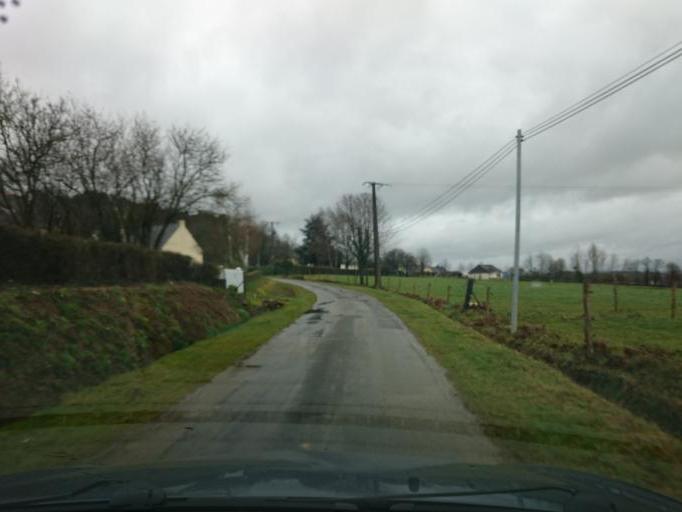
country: FR
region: Brittany
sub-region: Departement d'Ille-et-Vilaine
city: Chanteloup
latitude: 47.9429
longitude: -1.6150
